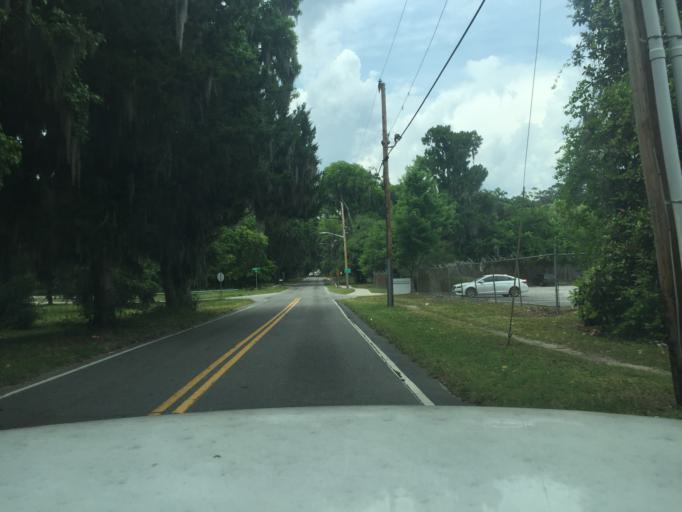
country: US
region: Georgia
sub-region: Chatham County
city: Thunderbolt
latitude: 32.0183
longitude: -81.0672
